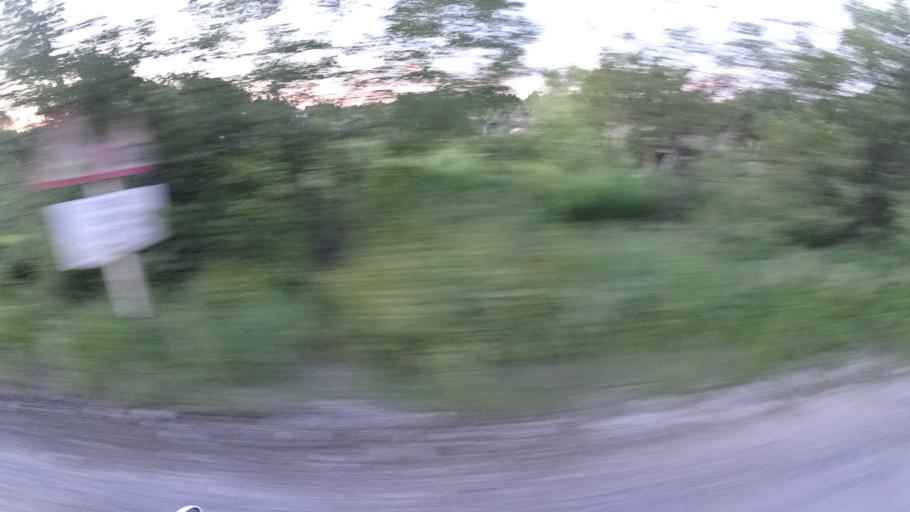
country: RU
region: Khabarovsk Krai
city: Khor
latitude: 47.8453
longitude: 134.9460
